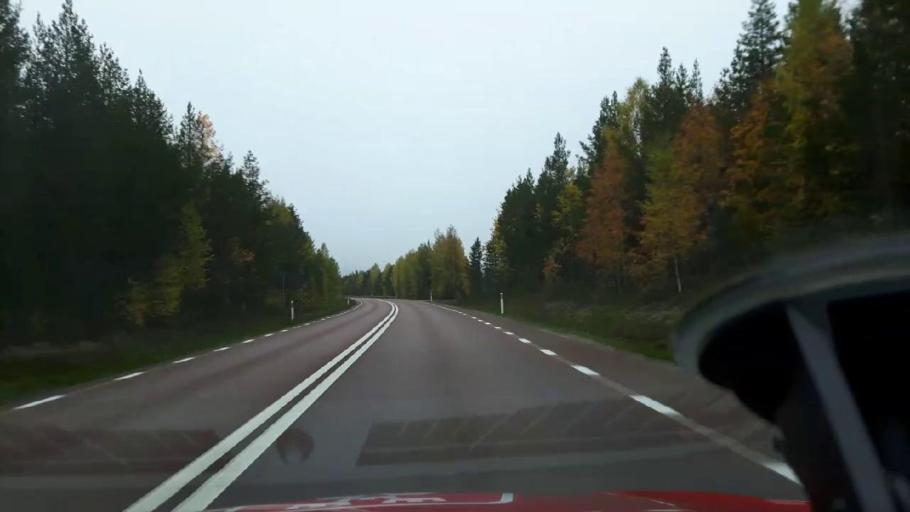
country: SE
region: Jaemtland
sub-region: Bergs Kommun
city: Hoverberg
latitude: 62.6184
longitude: 14.3777
